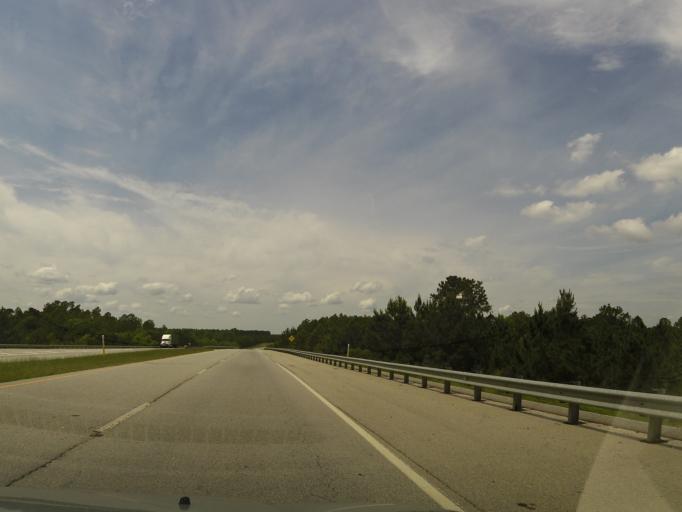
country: US
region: Georgia
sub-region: Emanuel County
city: Swainsboro
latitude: 32.5575
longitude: -82.3367
